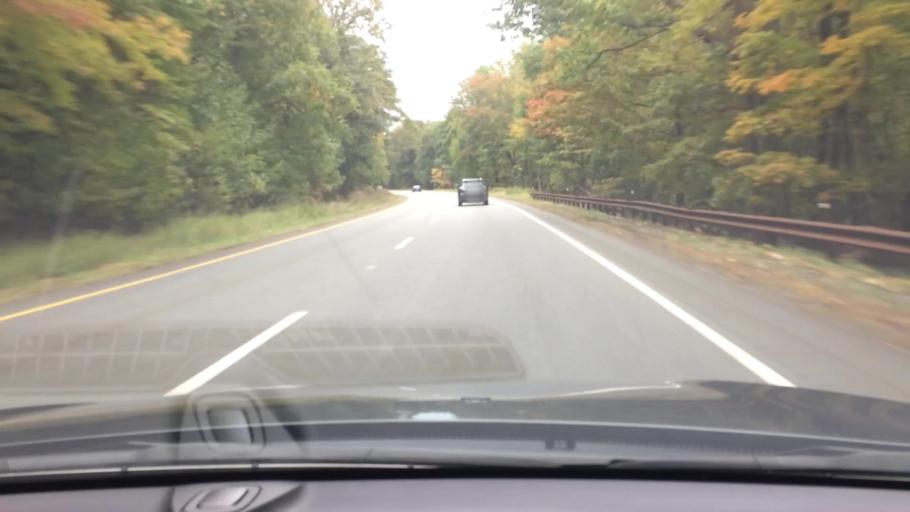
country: US
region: New Jersey
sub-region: Bergen County
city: Alpine
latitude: 40.9691
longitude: -73.9133
